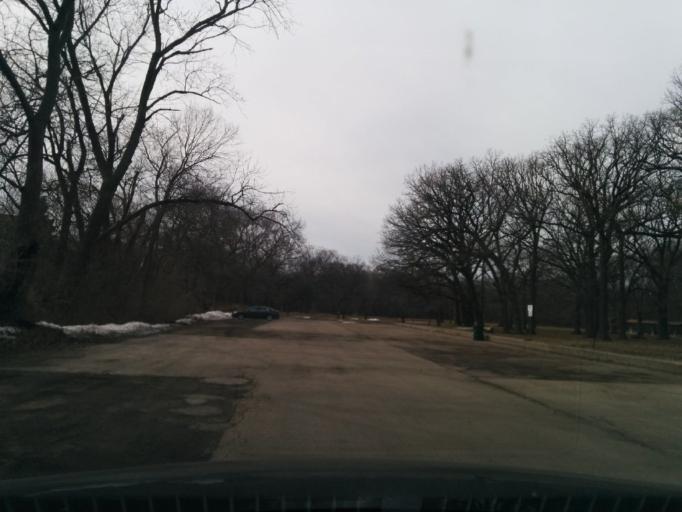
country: US
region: Illinois
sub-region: Cook County
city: Riverside
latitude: 41.8386
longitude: -87.8248
